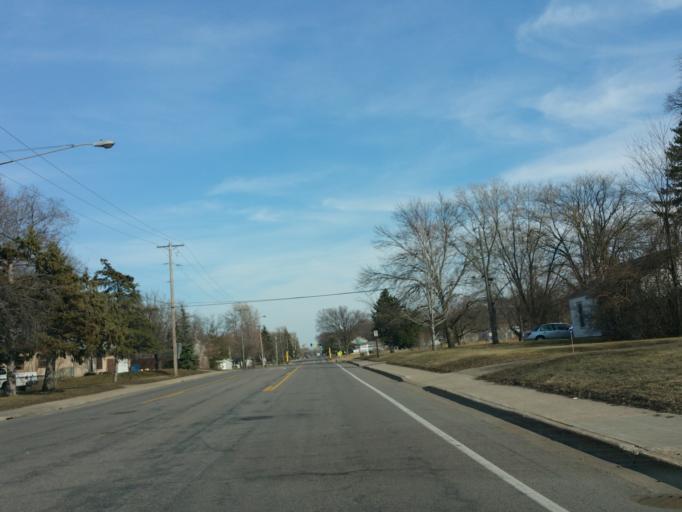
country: US
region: Minnesota
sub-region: Hennepin County
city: Bloomington
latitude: 44.8479
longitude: -93.2571
